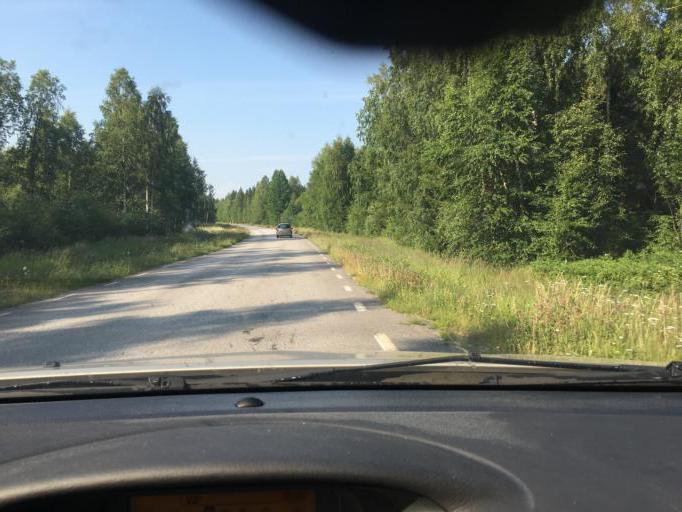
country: SE
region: Norrbotten
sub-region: Kalix Kommun
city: Toere
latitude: 65.8672
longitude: 22.6769
